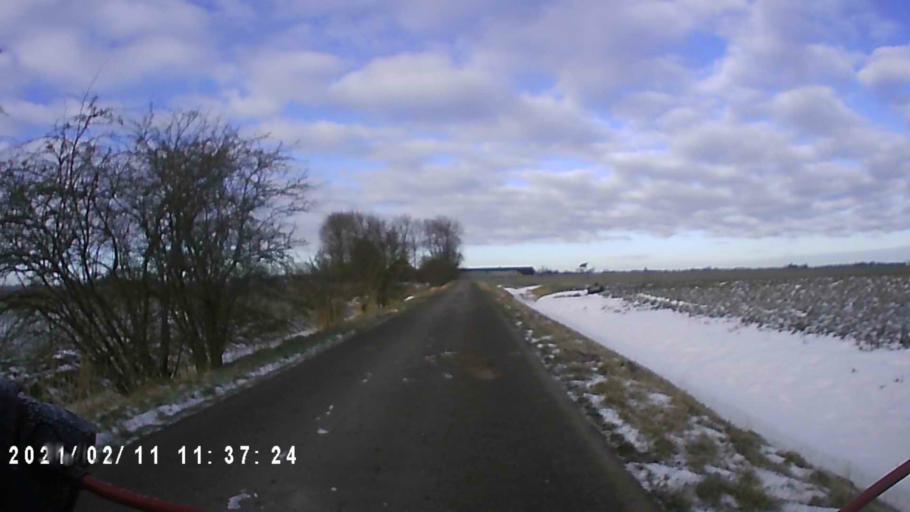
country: NL
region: Groningen
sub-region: Gemeente Zuidhorn
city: Aduard
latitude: 53.2862
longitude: 6.4693
